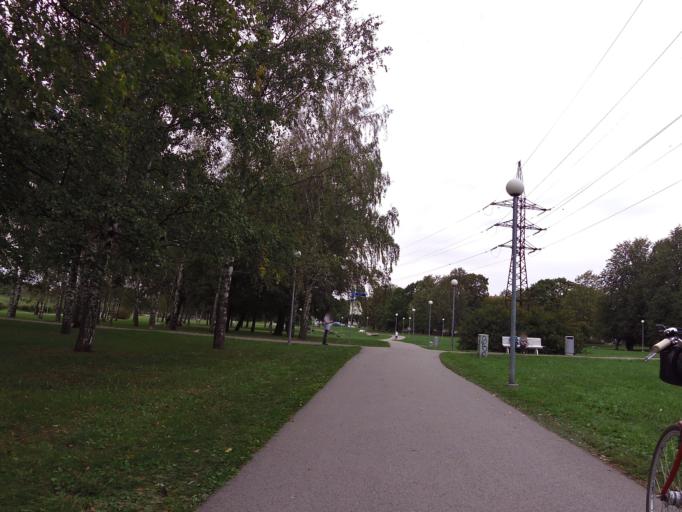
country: EE
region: Harju
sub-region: Tallinna linn
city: Tallinn
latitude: 59.4481
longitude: 24.6856
